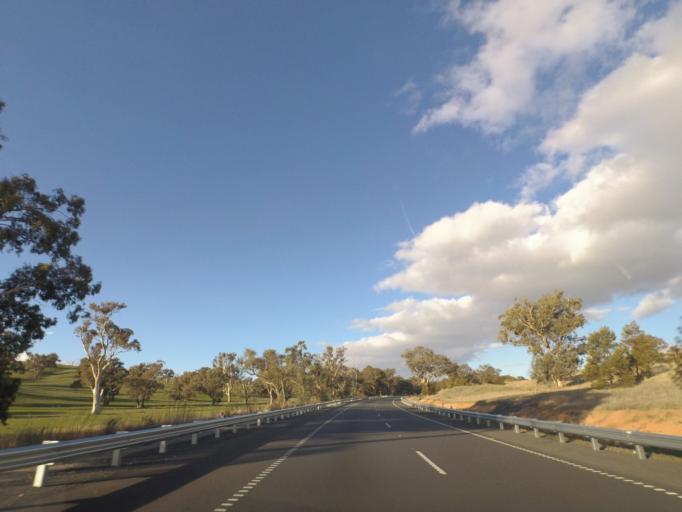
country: AU
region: New South Wales
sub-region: Gundagai
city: Gundagai
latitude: -34.8119
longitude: 148.4173
